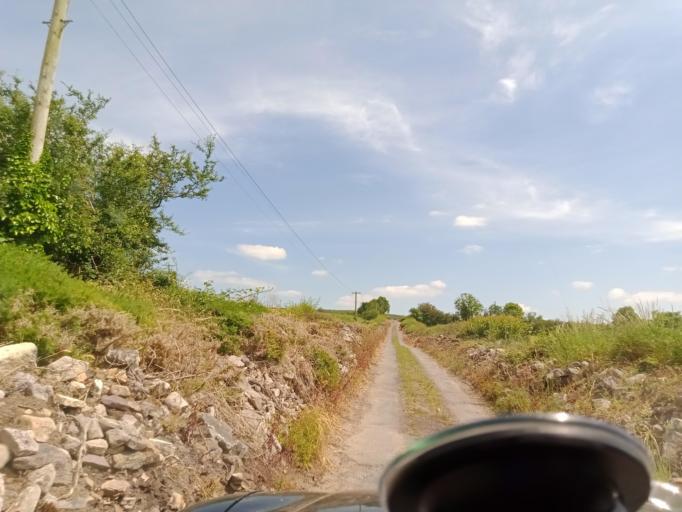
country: IE
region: Leinster
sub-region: Kilkenny
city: Thomastown
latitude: 52.5670
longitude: -7.0888
